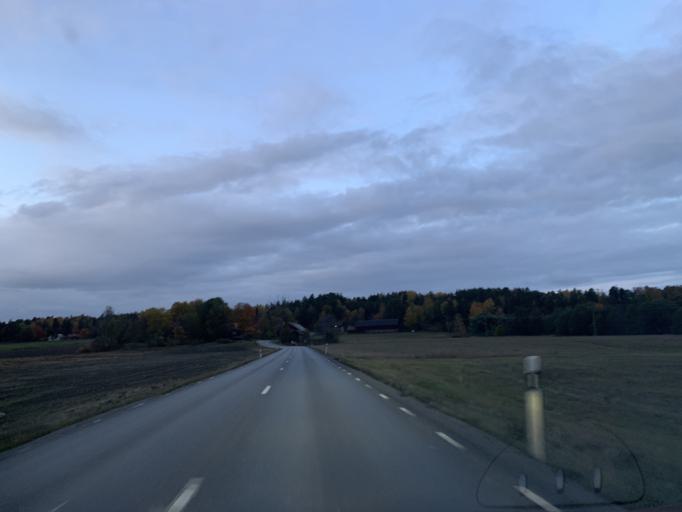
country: SE
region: Stockholm
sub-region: Botkyrka Kommun
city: Varsta
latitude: 59.0588
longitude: 17.8056
